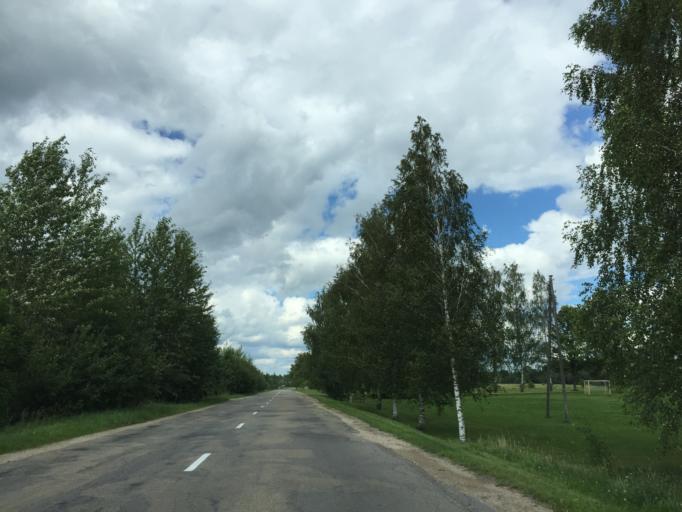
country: LV
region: Malpils
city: Malpils
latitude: 56.9133
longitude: 24.9320
